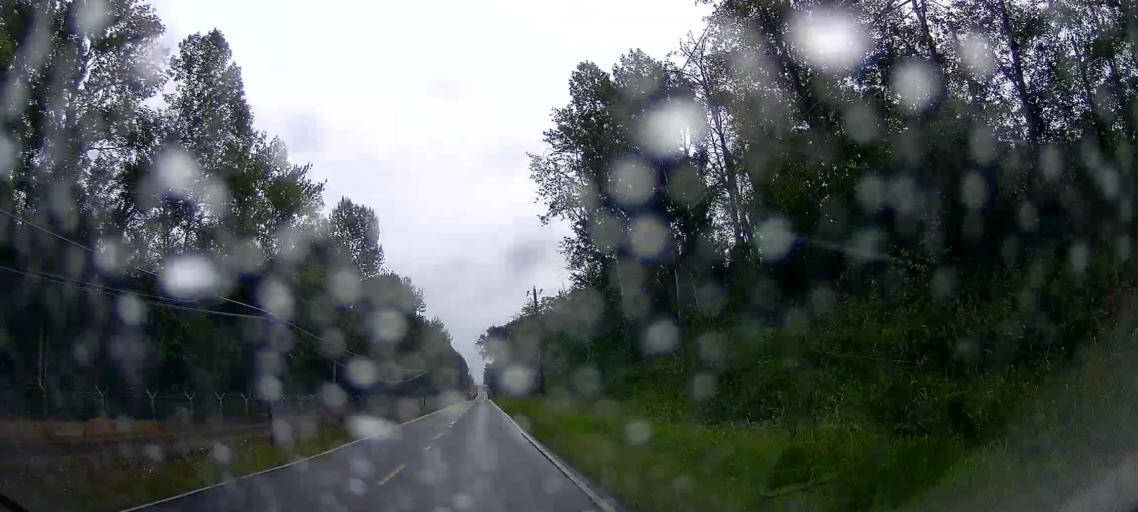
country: US
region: Washington
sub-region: Whatcom County
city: Ferndale
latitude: 48.8196
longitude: -122.6909
